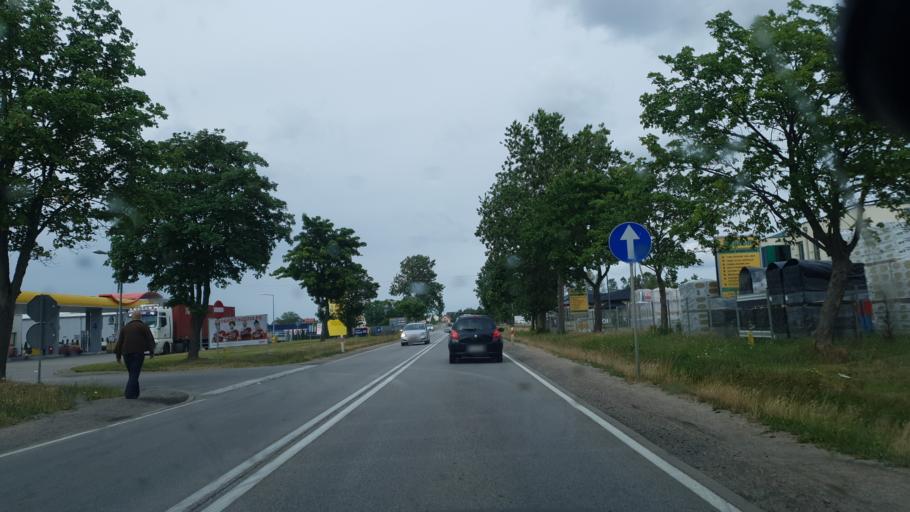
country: PL
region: Pomeranian Voivodeship
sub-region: Powiat kartuski
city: Banino
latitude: 54.4128
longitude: 18.3725
